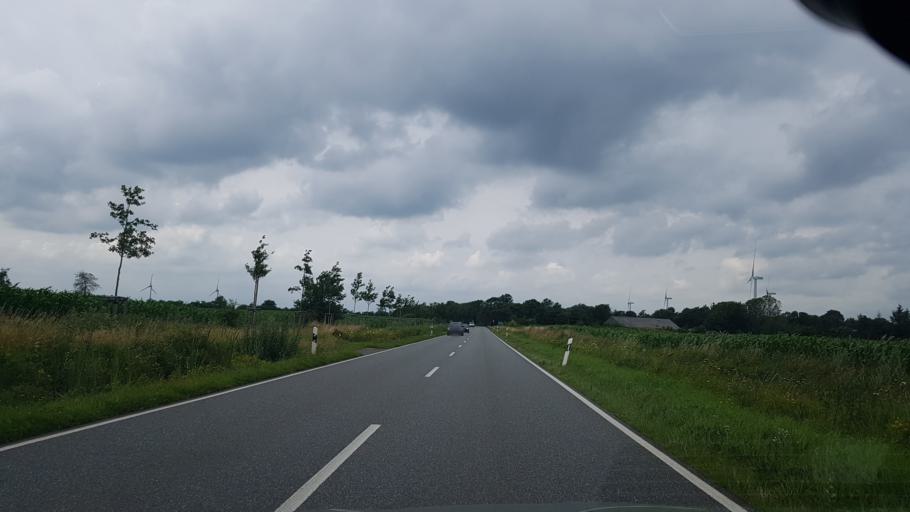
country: DE
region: Schleswig-Holstein
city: Boxlund
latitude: 54.8548
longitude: 9.1796
